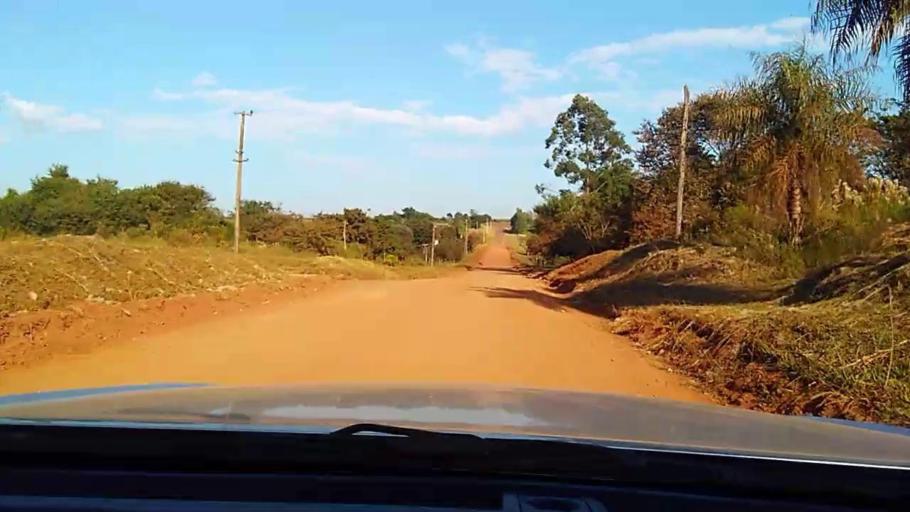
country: PY
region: Alto Parana
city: Santa Rita
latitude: -25.7066
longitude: -55.3838
